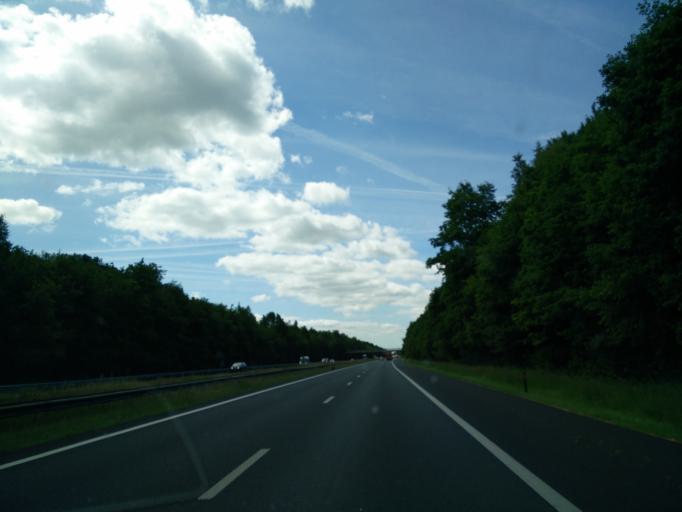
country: NL
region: Drenthe
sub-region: Gemeente Assen
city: Assen
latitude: 52.9283
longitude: 6.5352
